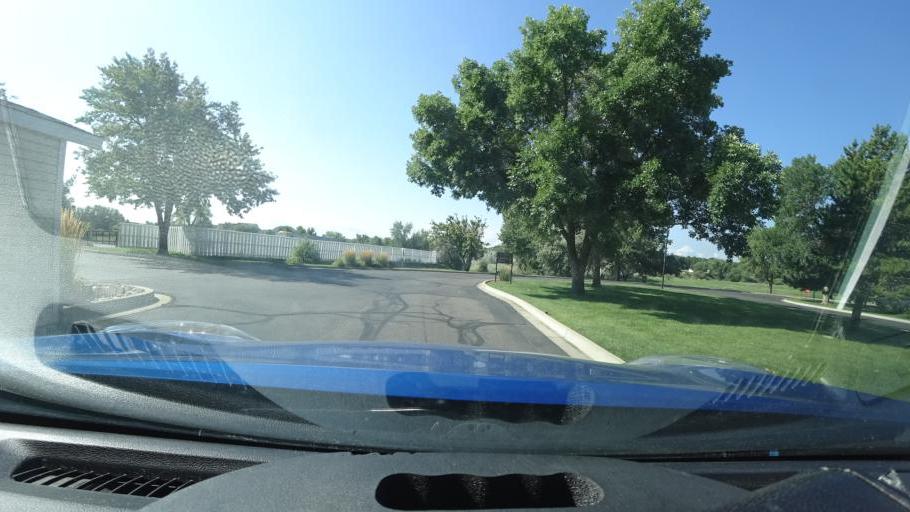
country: US
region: Colorado
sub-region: Adams County
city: Aurora
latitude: 39.7230
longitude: -104.8129
